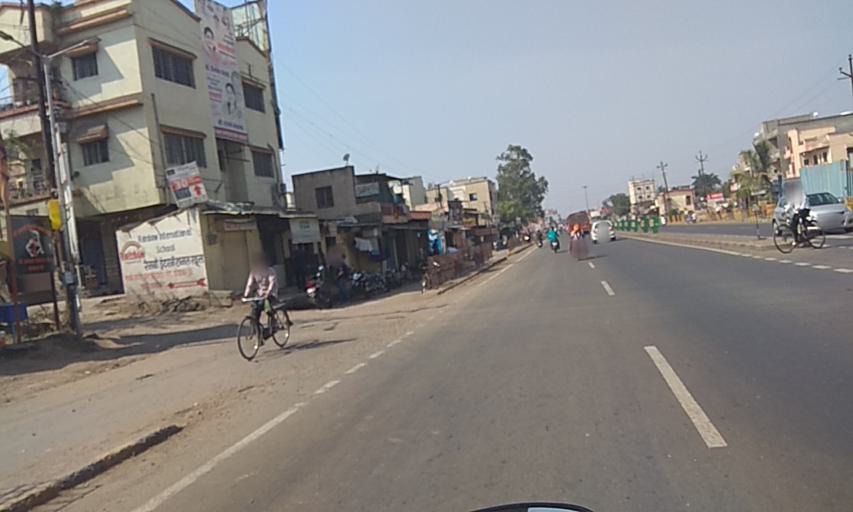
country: IN
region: Maharashtra
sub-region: Pune Division
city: Lohogaon
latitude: 18.4911
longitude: 74.0080
